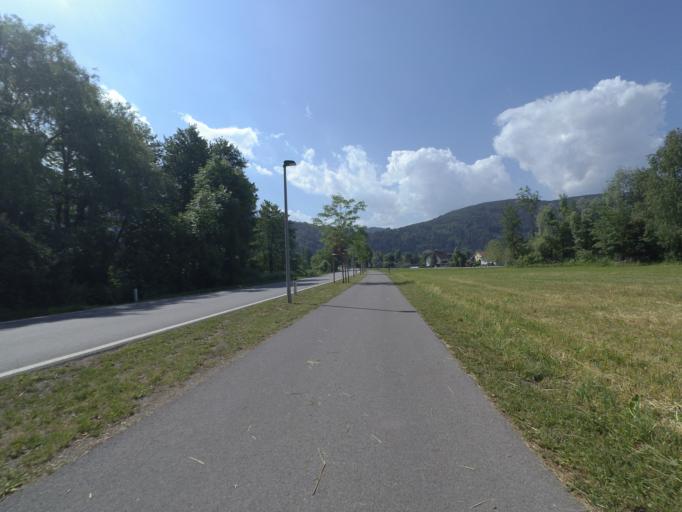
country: AT
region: Carinthia
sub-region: Politischer Bezirk Villach Land
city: Ferndorf
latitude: 46.7756
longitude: 13.6444
